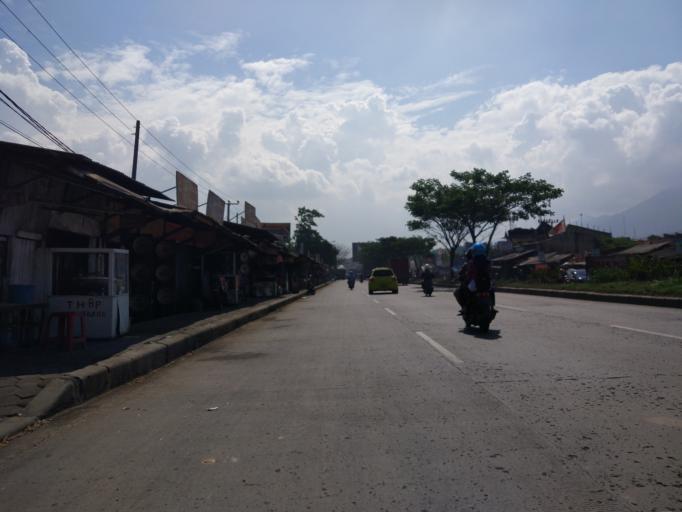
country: ID
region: West Java
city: Cileunyi
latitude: -6.9441
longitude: 107.7571
